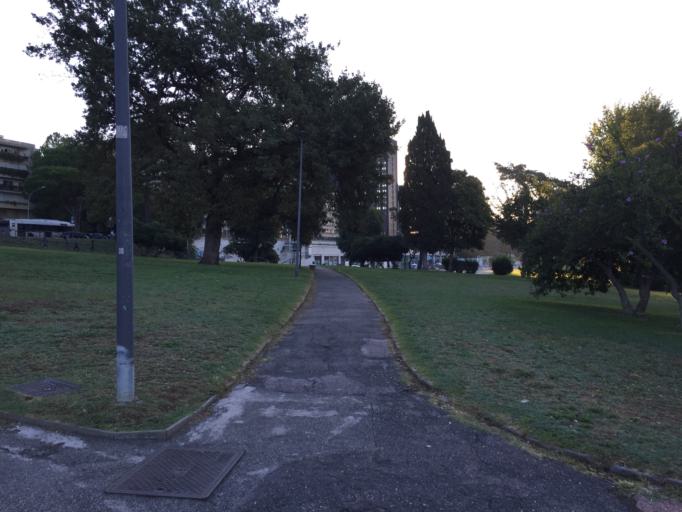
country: IT
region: Latium
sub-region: Citta metropolitana di Roma Capitale
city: Selcetta
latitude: 41.8301
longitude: 12.4639
